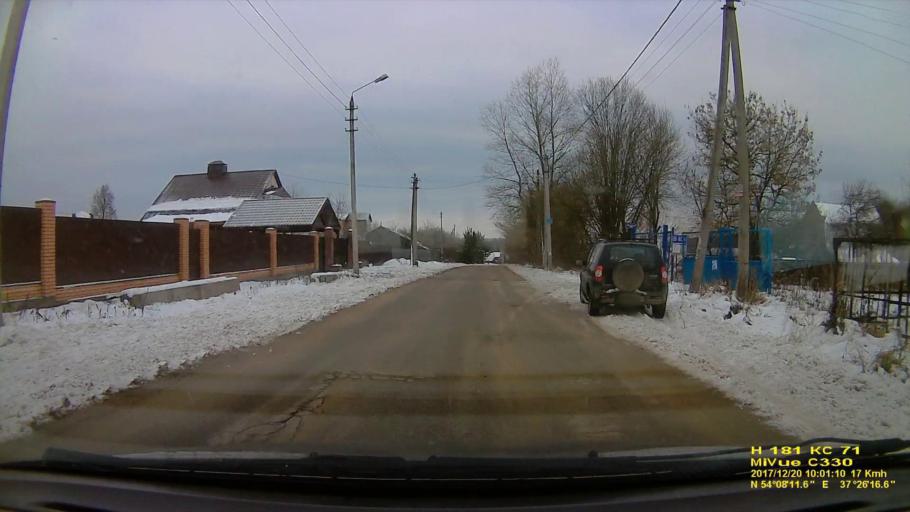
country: RU
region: Tula
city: Kosaya Gora
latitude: 54.1366
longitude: 37.4379
